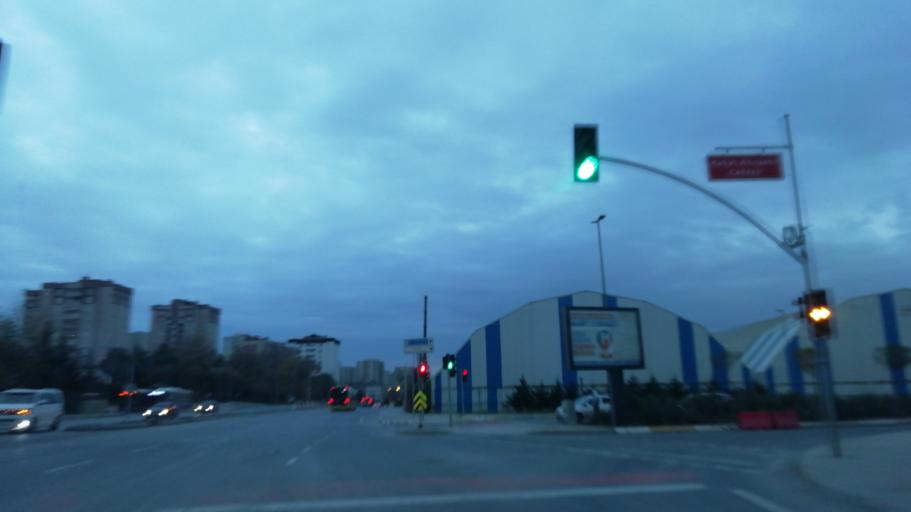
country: TR
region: Istanbul
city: Basaksehir
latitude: 41.0584
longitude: 28.7743
